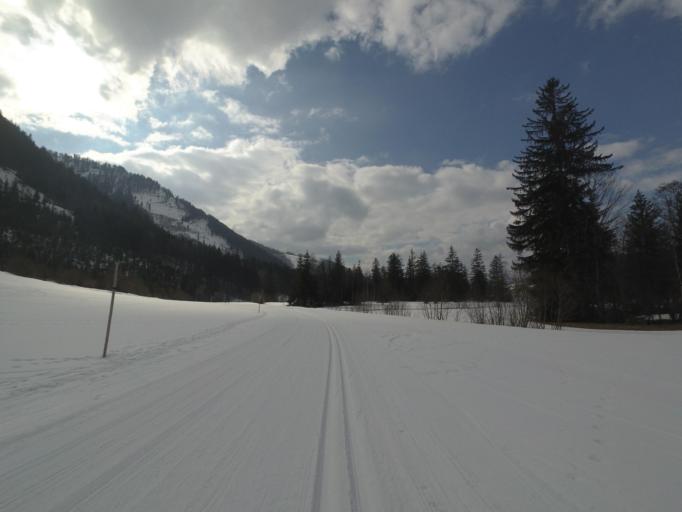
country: AT
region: Salzburg
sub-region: Politischer Bezirk Salzburg-Umgebung
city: Faistenau
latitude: 47.7663
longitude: 13.2715
